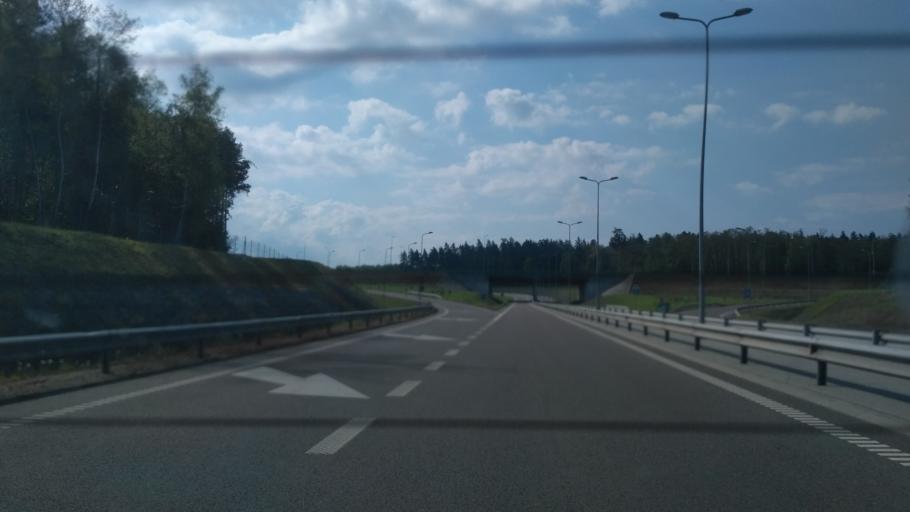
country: PL
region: Subcarpathian Voivodeship
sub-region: Powiat lubaczowski
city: Wielkie Oczy
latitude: 49.9654
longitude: 23.0684
